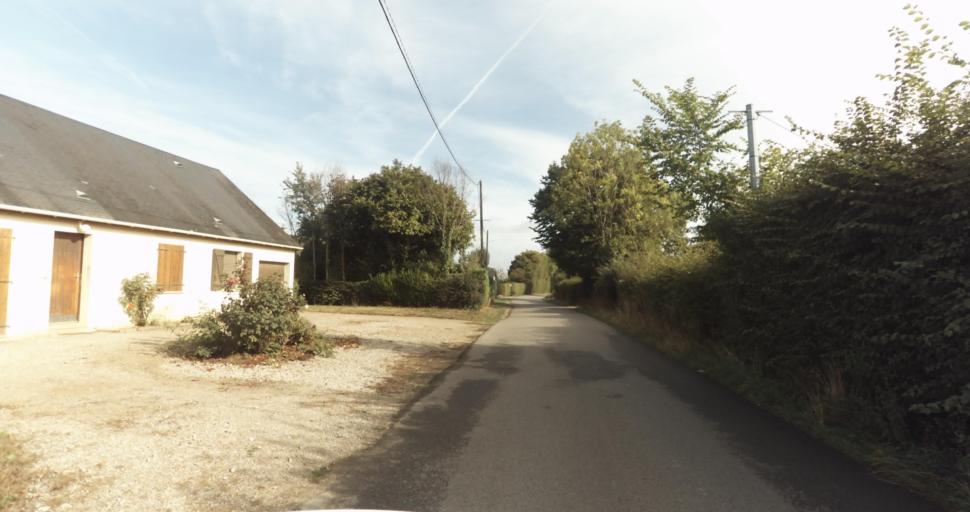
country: FR
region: Lower Normandy
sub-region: Departement de l'Orne
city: Gace
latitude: 48.8963
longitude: 0.3415
